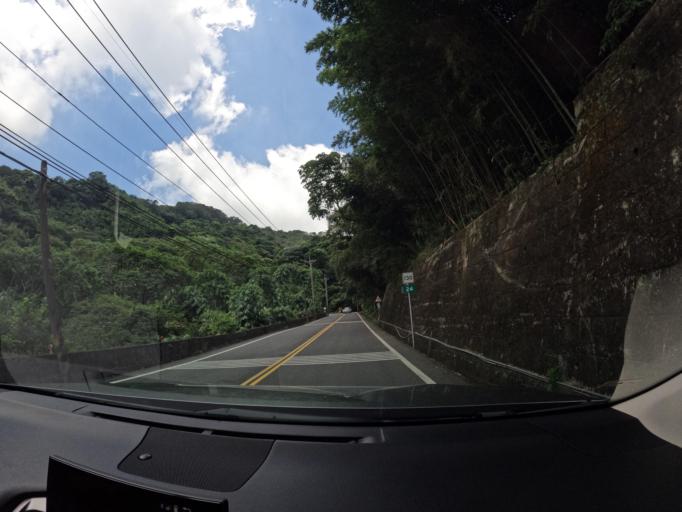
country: TW
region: Taiwan
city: Fengyuan
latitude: 24.3841
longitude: 120.8159
